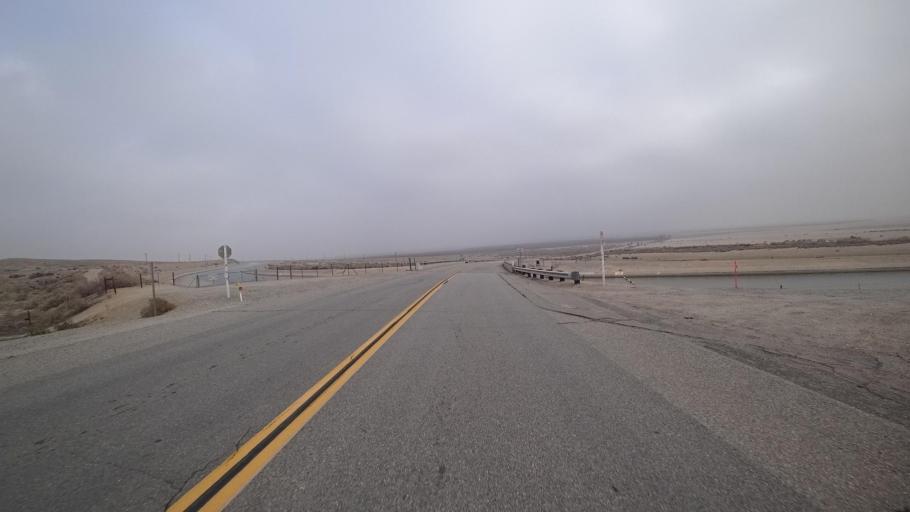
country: US
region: California
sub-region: Kern County
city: Maricopa
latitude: 35.1300
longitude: -119.3692
